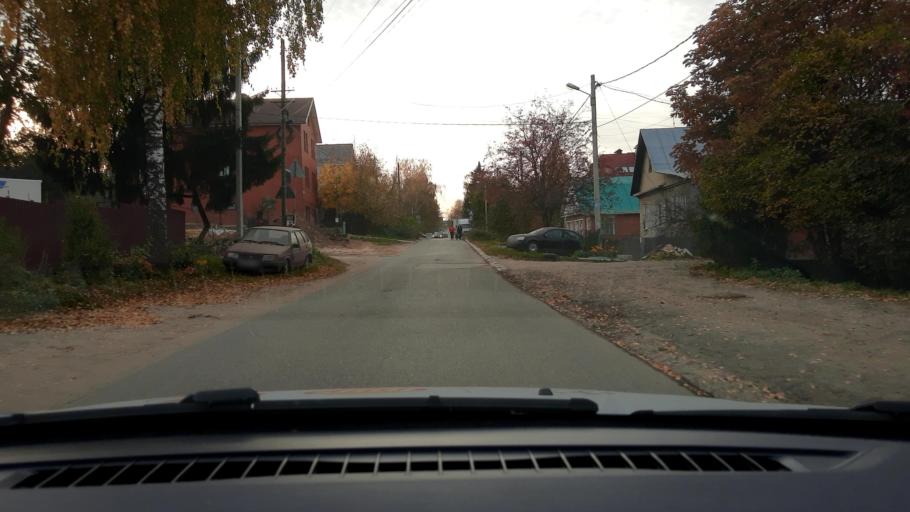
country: RU
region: Nizjnij Novgorod
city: Nizhniy Novgorod
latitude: 56.2740
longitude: 44.0083
